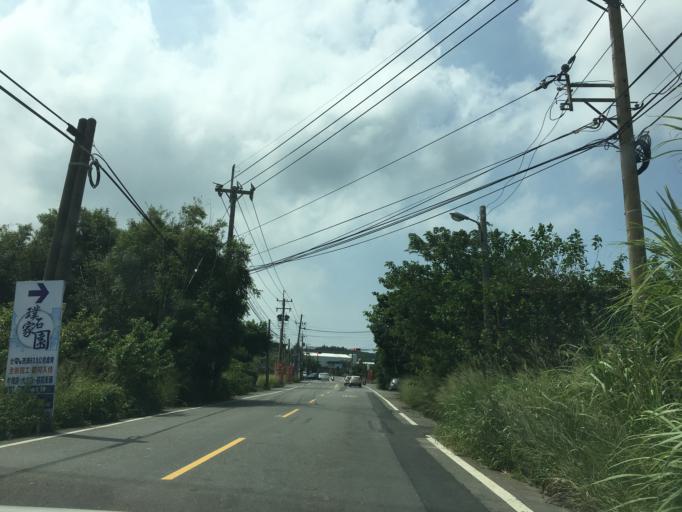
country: TW
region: Taiwan
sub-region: Hsinchu
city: Zhubei
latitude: 24.8943
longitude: 120.9772
